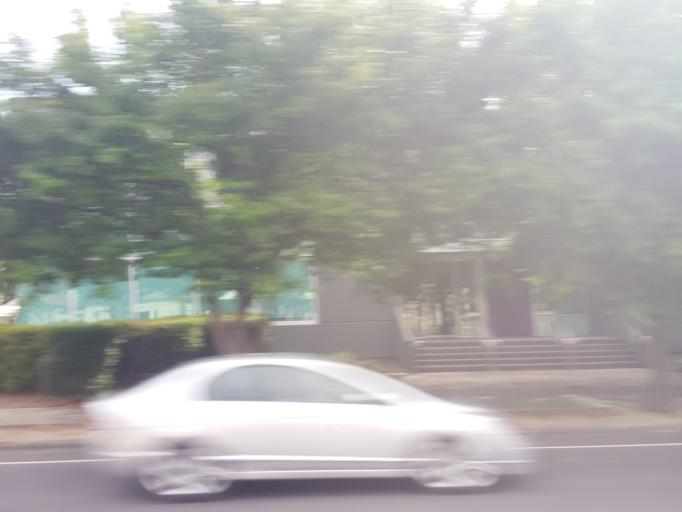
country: AU
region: South Australia
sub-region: Charles Sturt
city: Allenby Gardens
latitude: -34.8893
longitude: 138.5717
